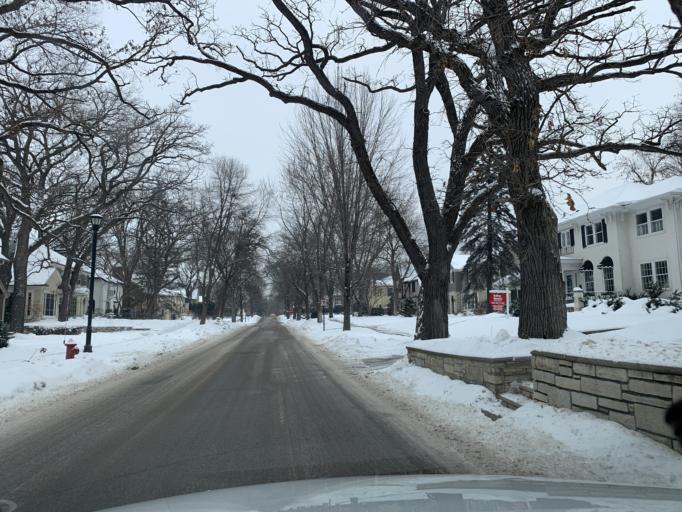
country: US
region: Minnesota
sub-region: Hennepin County
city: Edina
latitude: 44.9172
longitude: -93.3440
